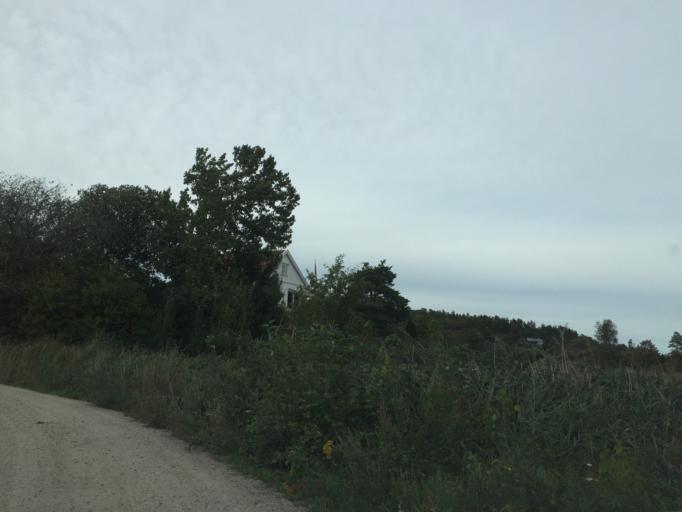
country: NO
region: Ostfold
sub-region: Hvaler
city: Skjaerhalden
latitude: 59.0364
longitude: 11.0533
